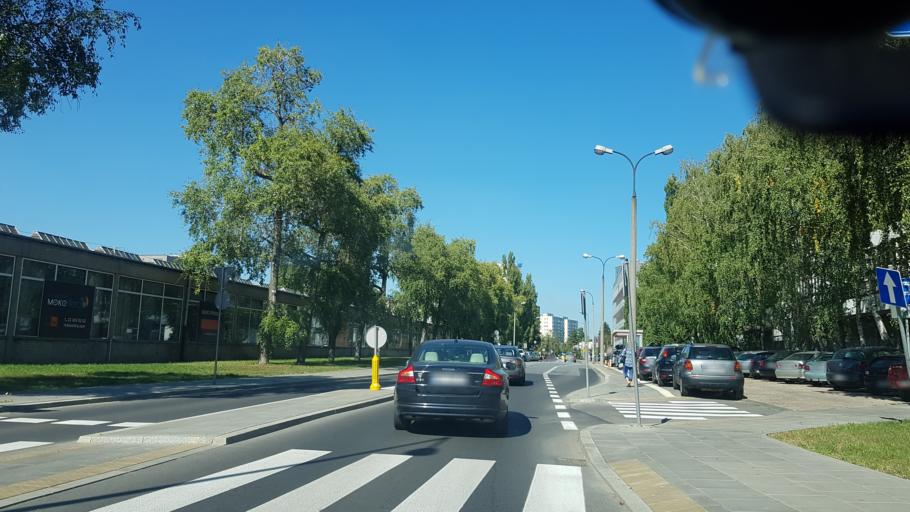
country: PL
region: Masovian Voivodeship
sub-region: Warszawa
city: Ochota
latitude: 52.1856
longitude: 20.9930
